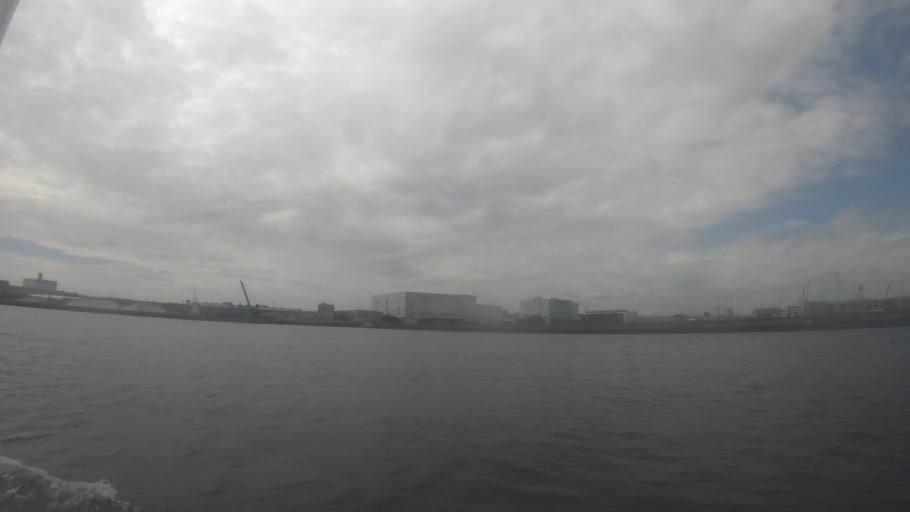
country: JP
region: Kanagawa
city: Yokohama
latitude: 35.3768
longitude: 139.6517
